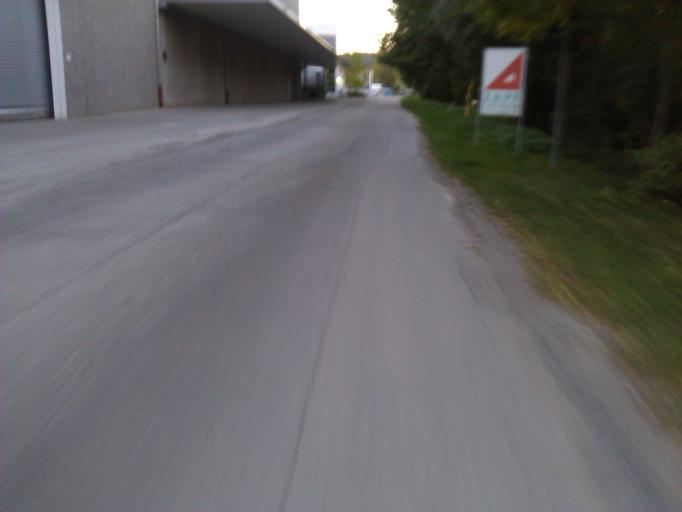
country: DE
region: Baden-Wuerttemberg
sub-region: Karlsruhe Region
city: Zuzenhausen
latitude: 49.2676
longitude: 8.8399
